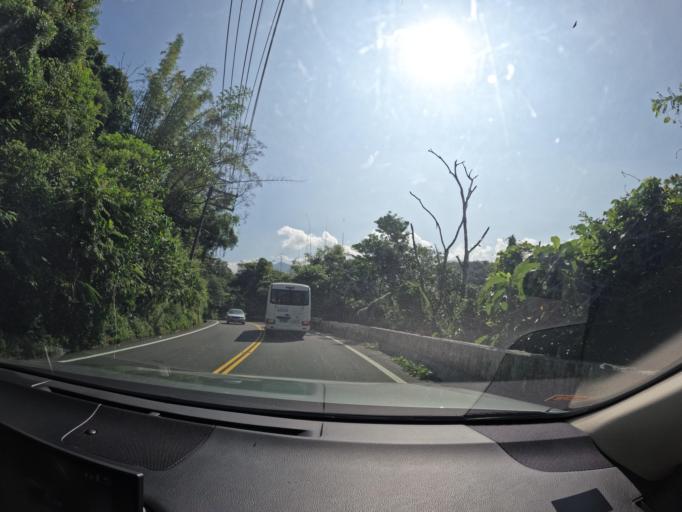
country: TW
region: Taiwan
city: Yujing
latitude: 23.0692
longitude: 120.6471
